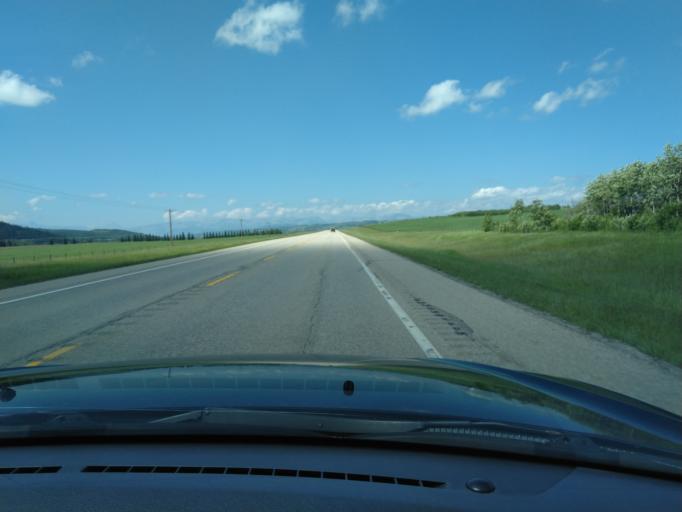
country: CA
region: Alberta
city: Cochrane
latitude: 51.2242
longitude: -114.6593
